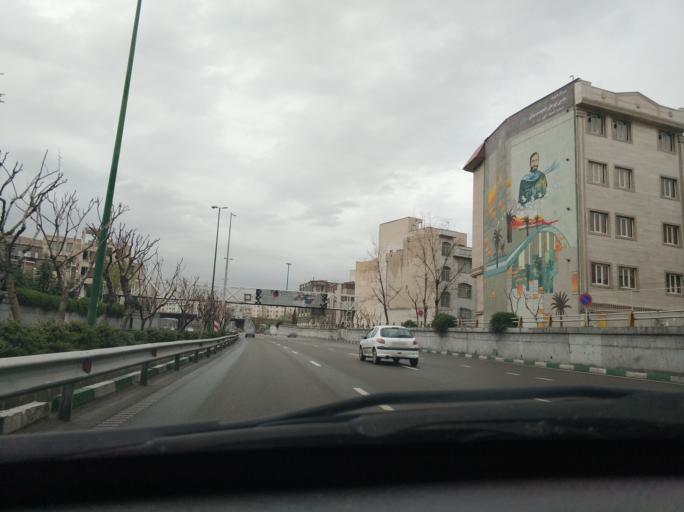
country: IR
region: Tehran
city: Tehran
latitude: 35.7259
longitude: 51.4567
